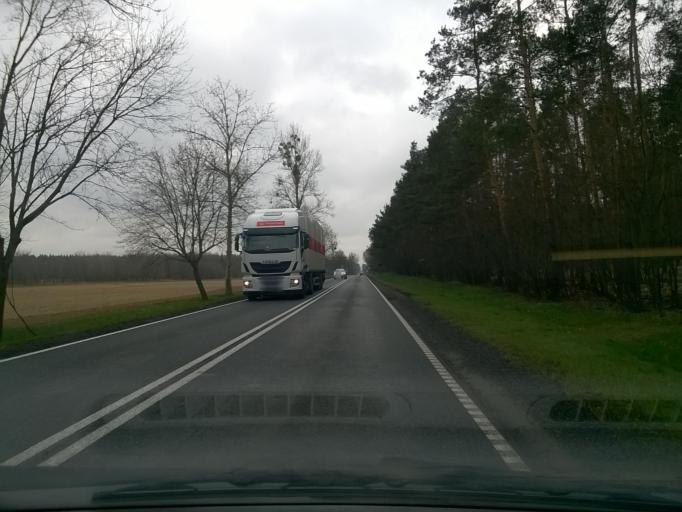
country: PL
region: Kujawsko-Pomorskie
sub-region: Powiat zninski
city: Znin
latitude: 52.9337
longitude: 17.6962
